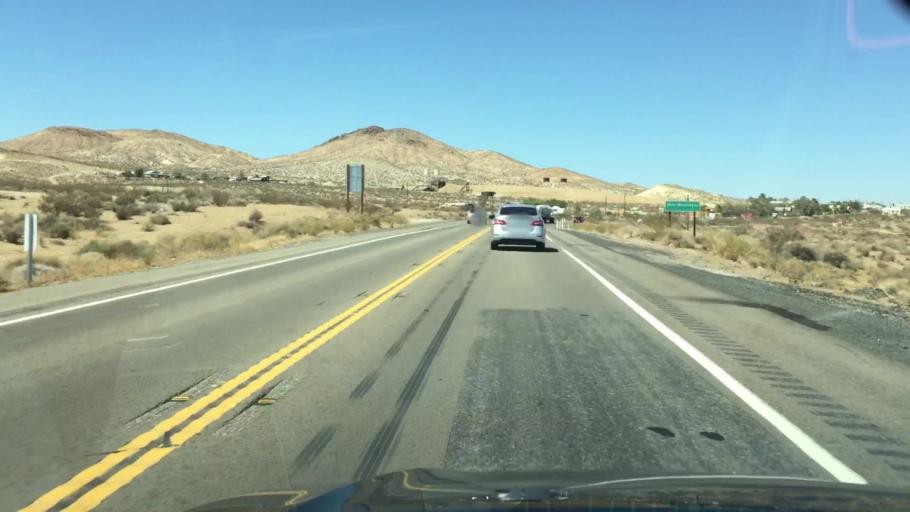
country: US
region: California
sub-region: Kern County
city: Ridgecrest
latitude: 35.3437
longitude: -117.6209
